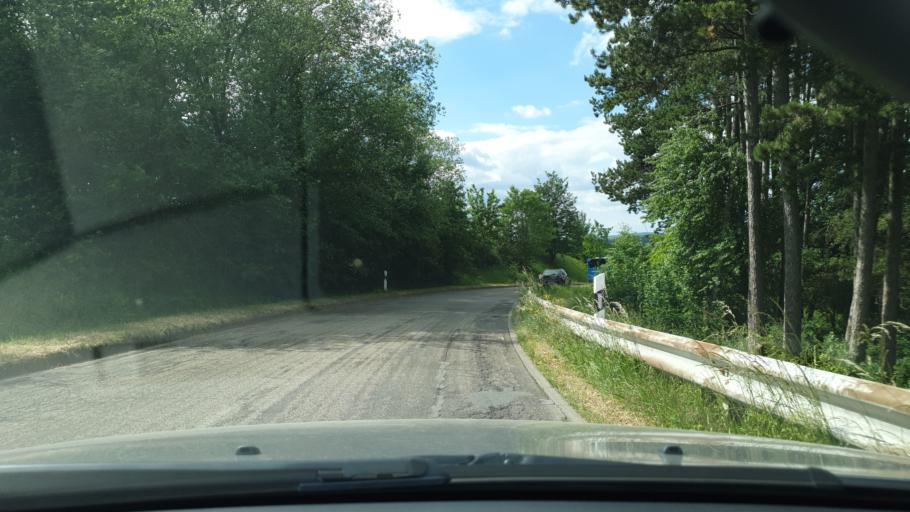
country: DE
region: Rheinland-Pfalz
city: Contwig
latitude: 49.2670
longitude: 7.4335
